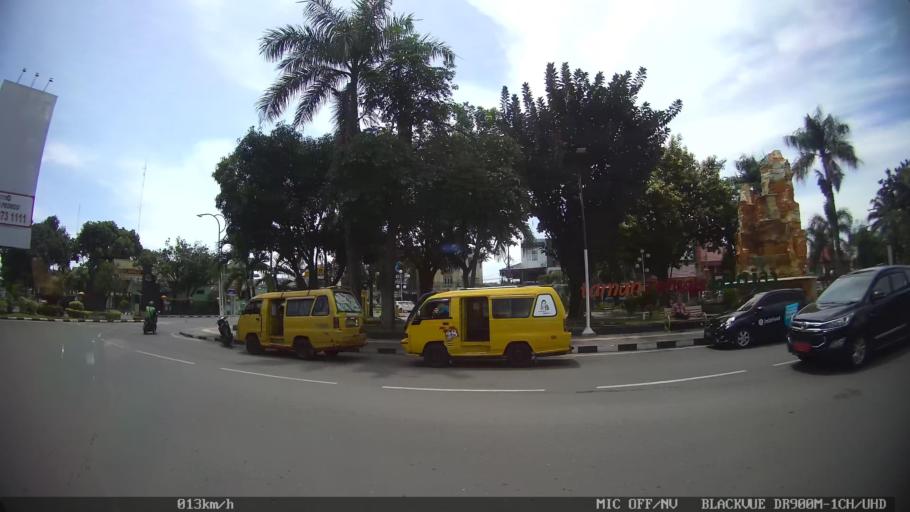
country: ID
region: North Sumatra
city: Binjai
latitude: 3.6020
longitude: 98.4808
